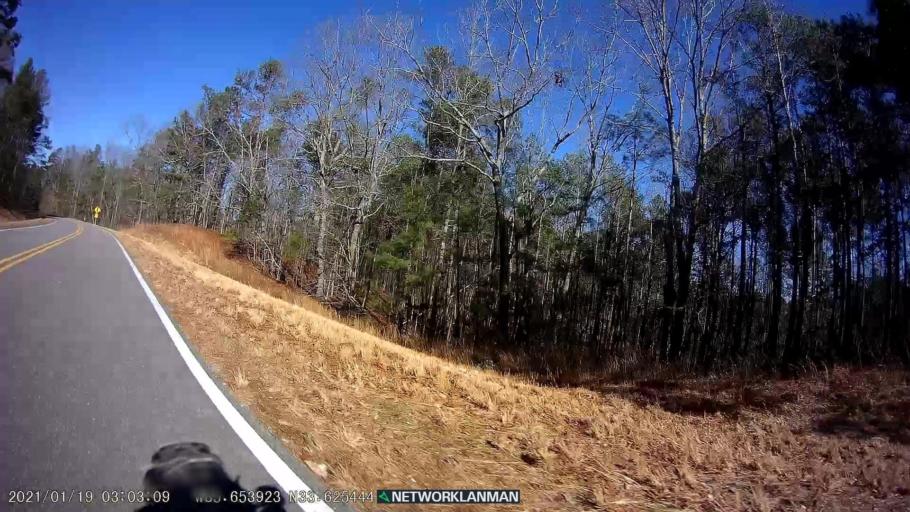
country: US
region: Alabama
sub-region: Calhoun County
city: Choccolocco
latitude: 33.6253
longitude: -85.6536
